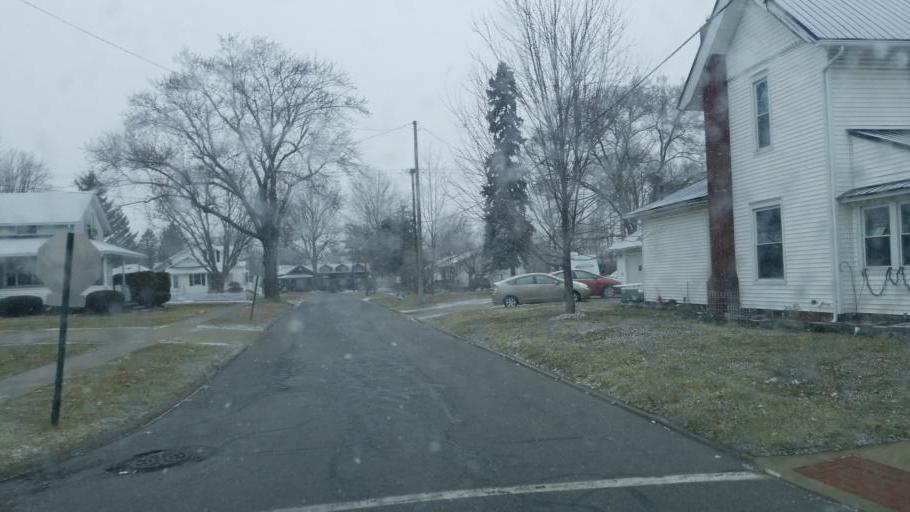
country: US
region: Ohio
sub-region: Defiance County
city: Hicksville
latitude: 41.2958
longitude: -84.7616
